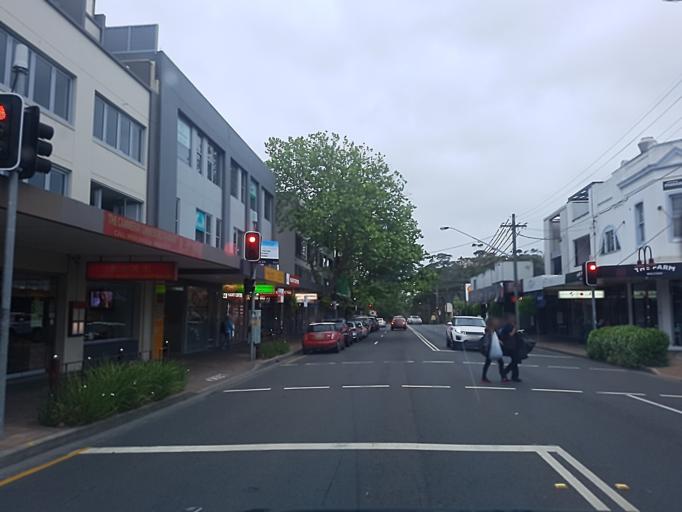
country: AU
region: New South Wales
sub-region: North Sydney
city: Cammeray
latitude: -33.8221
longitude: 151.2104
